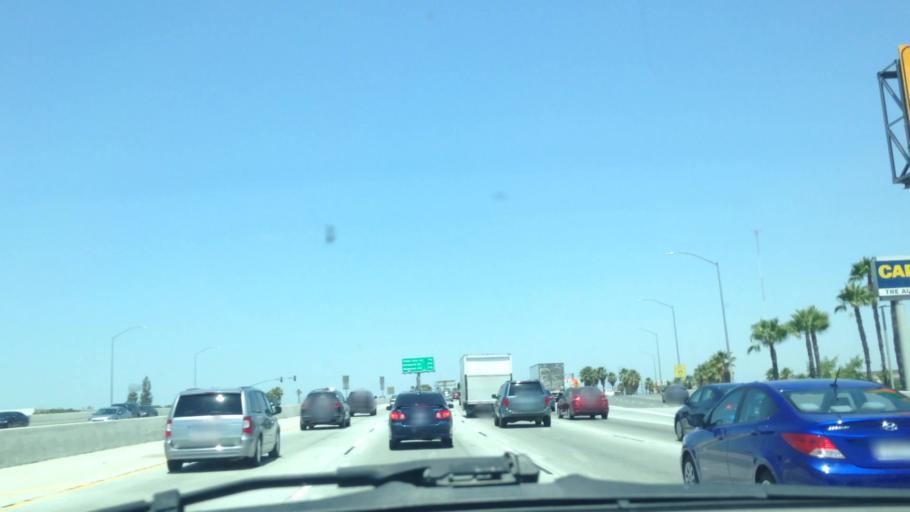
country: US
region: California
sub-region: Orange County
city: Buena Park
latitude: 33.8715
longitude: -118.0051
